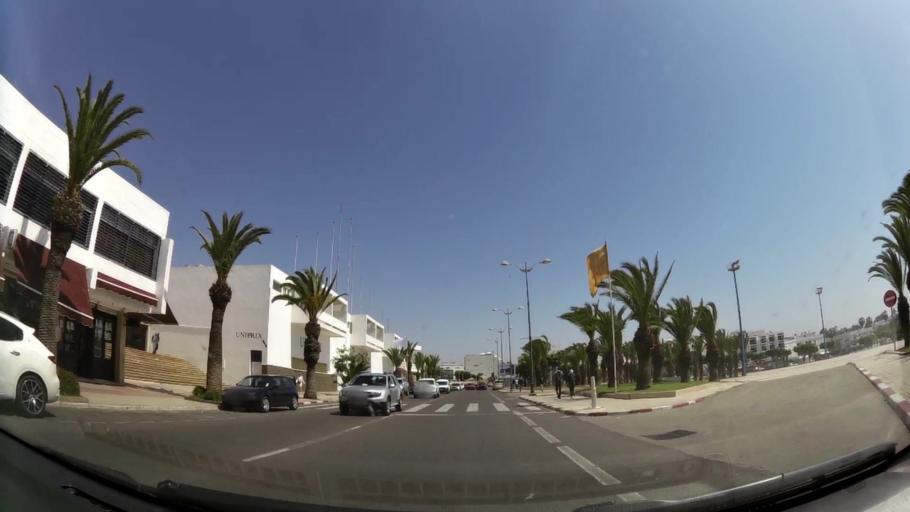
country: MA
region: Souss-Massa-Draa
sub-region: Agadir-Ida-ou-Tnan
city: Agadir
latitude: 30.4209
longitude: -9.6000
